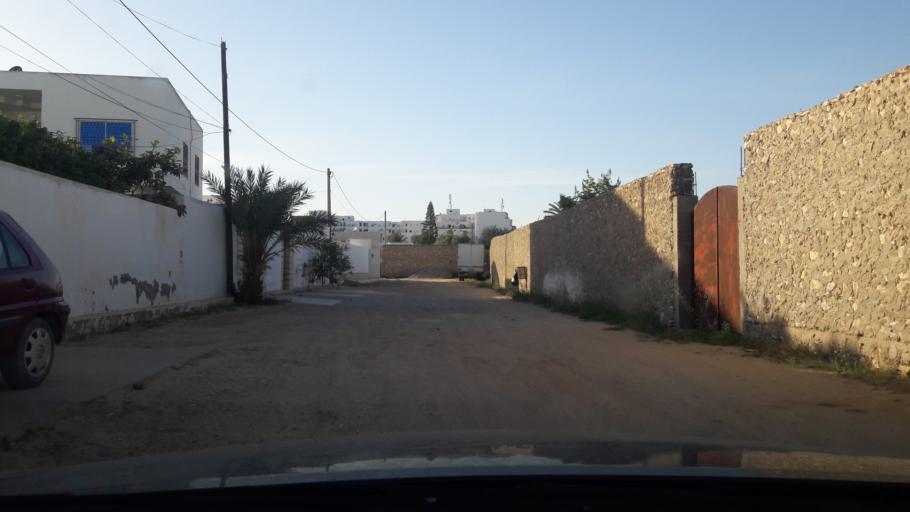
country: TN
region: Safaqis
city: Al Qarmadah
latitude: 34.7957
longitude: 10.7590
